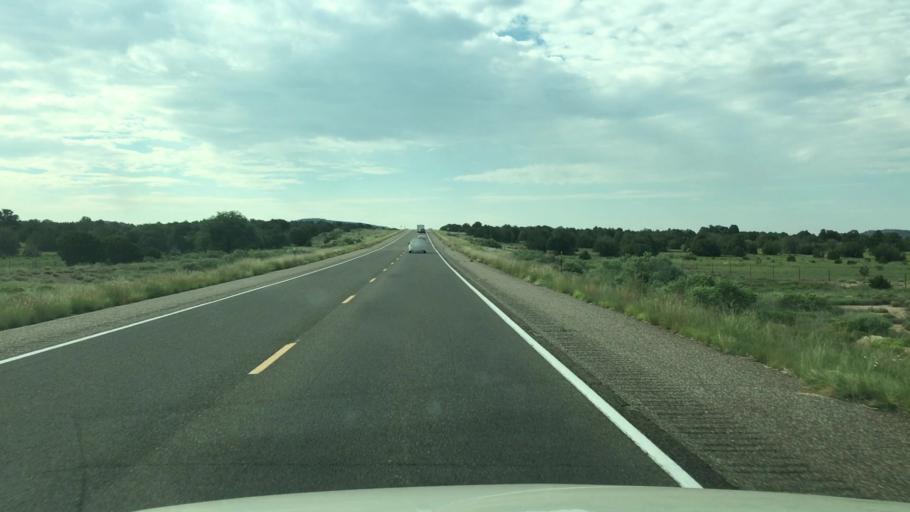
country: US
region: New Mexico
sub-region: Santa Fe County
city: Eldorado at Santa Fe
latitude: 35.3379
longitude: -105.8387
